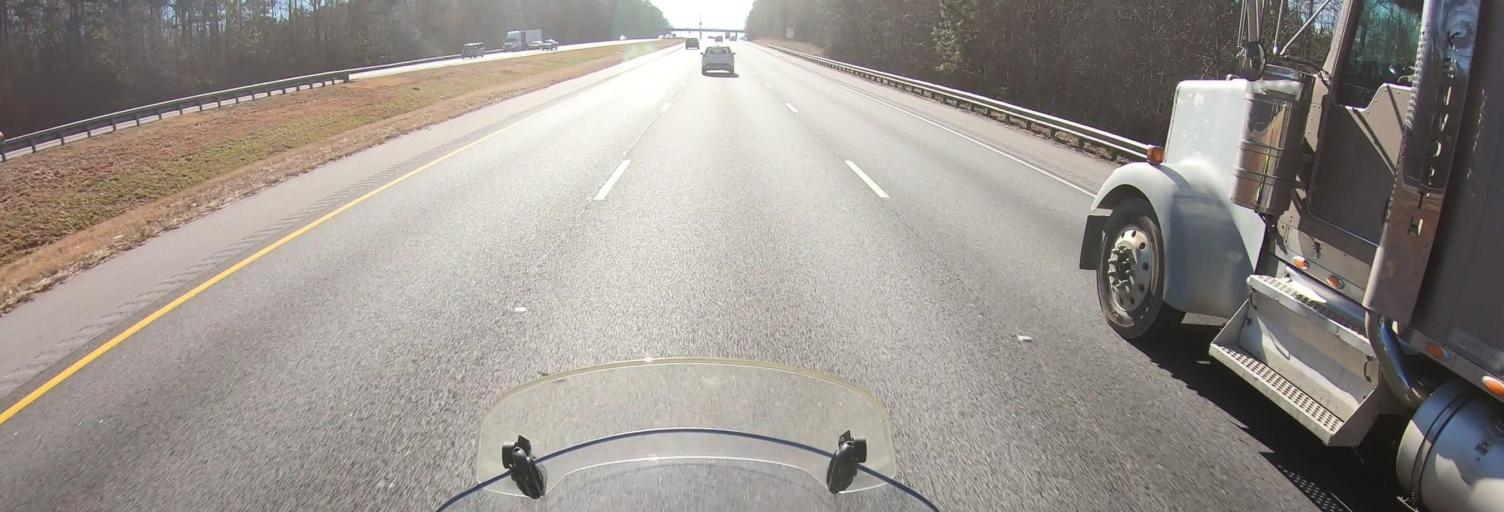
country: US
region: Georgia
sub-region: Henry County
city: Locust Grove
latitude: 33.3807
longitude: -84.1424
